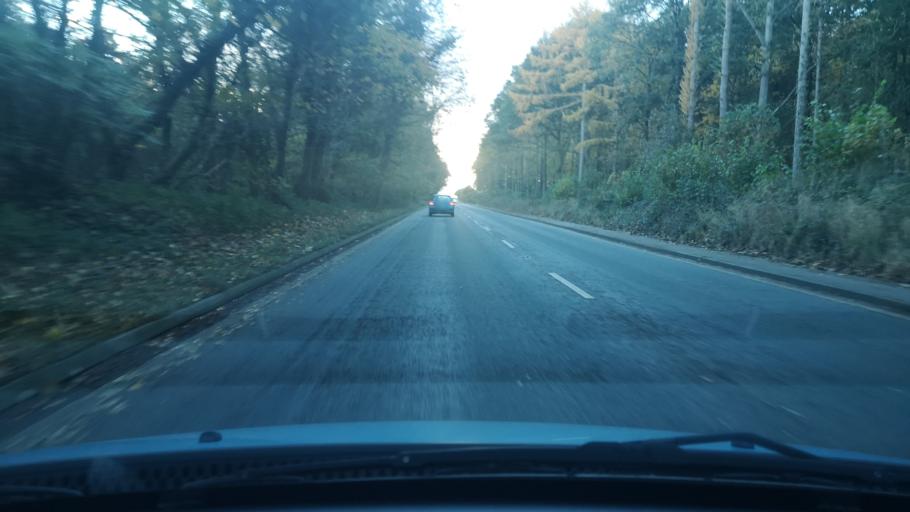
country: GB
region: England
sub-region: City and Borough of Wakefield
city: Horbury
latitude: 53.6336
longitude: -1.5579
